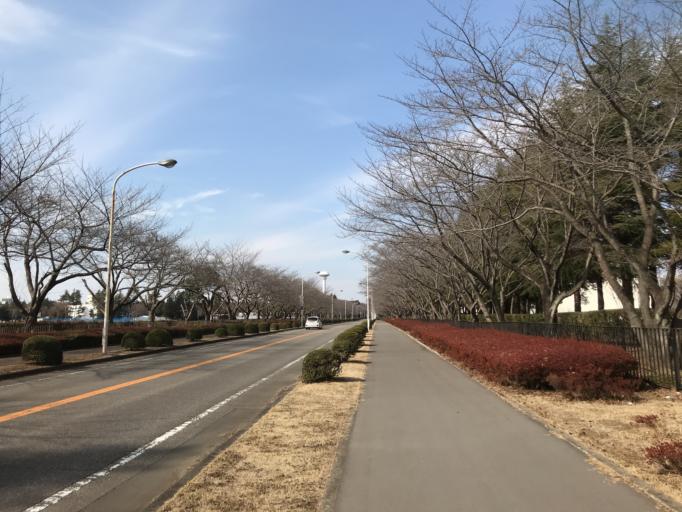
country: JP
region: Ibaraki
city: Naka
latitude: 36.0275
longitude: 140.1081
